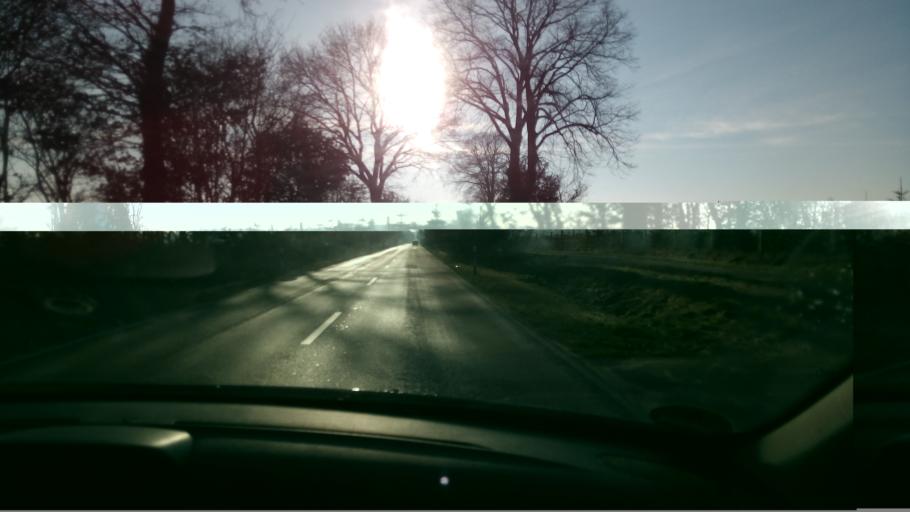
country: DE
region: Schleswig-Holstein
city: Witzeeze
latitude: 53.4467
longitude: 10.6102
